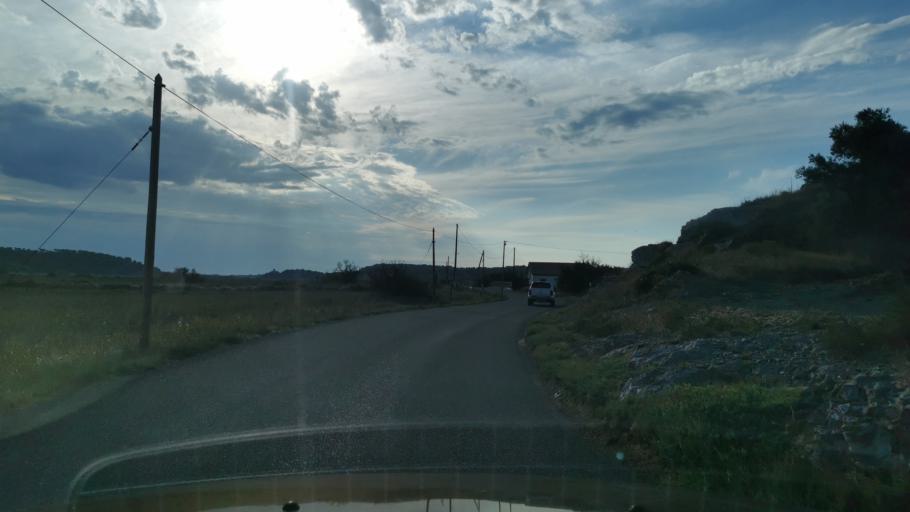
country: FR
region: Languedoc-Roussillon
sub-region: Departement de l'Aude
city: Gruissan
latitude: 43.1133
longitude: 3.0450
